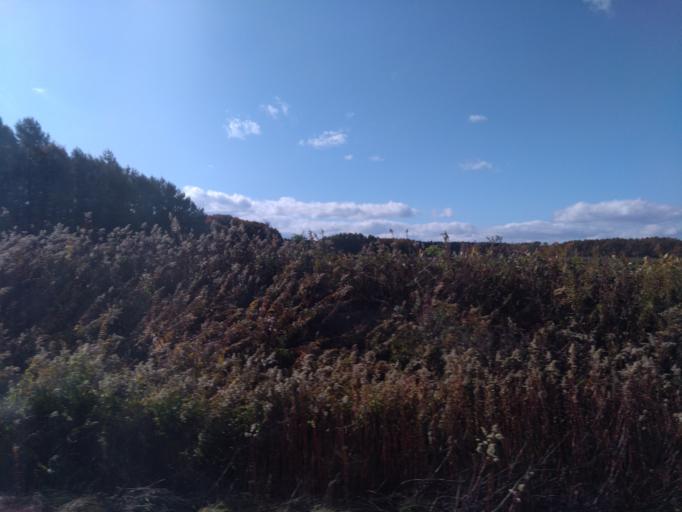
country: JP
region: Hokkaido
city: Kitahiroshima
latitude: 42.9509
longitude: 141.5709
